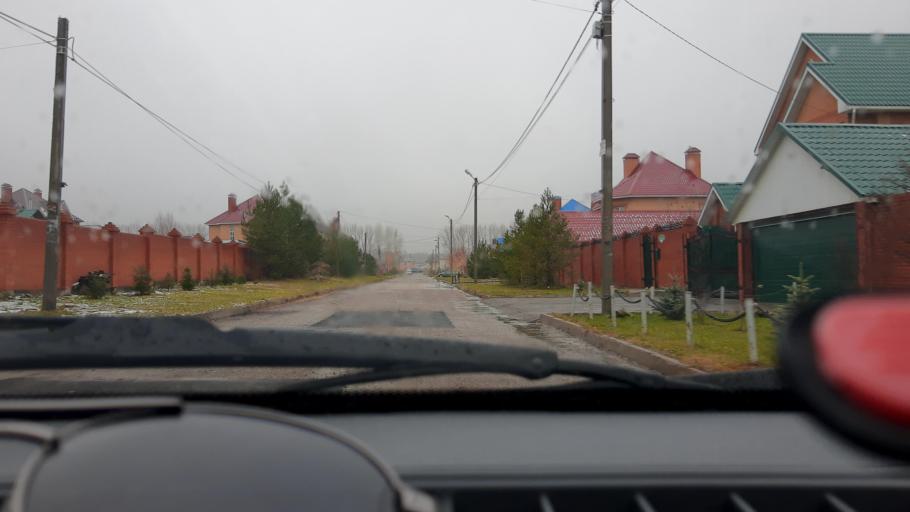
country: RU
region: Bashkortostan
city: Kabakovo
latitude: 54.6219
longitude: 56.1228
